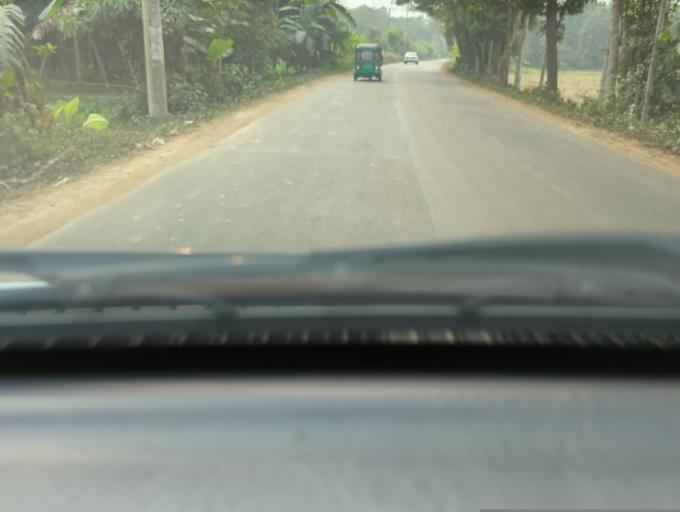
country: BD
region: Sylhet
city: Maulavi Bazar
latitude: 24.5268
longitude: 91.7336
